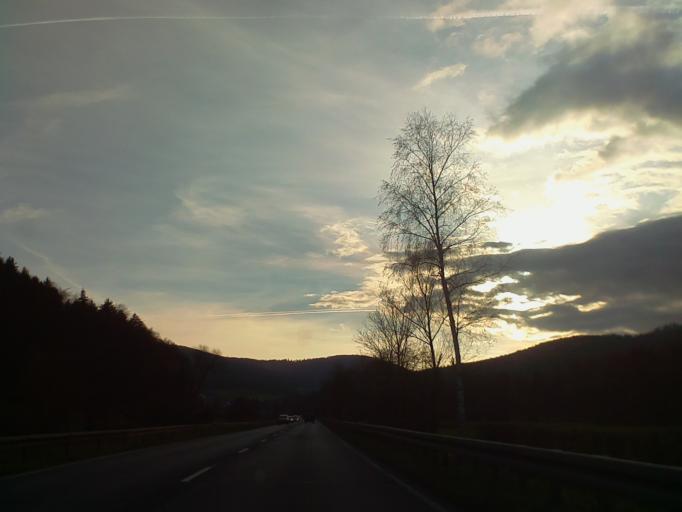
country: DE
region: Bavaria
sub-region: Regierungsbezirk Unterfranken
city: Weilbach
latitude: 49.6602
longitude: 9.2112
